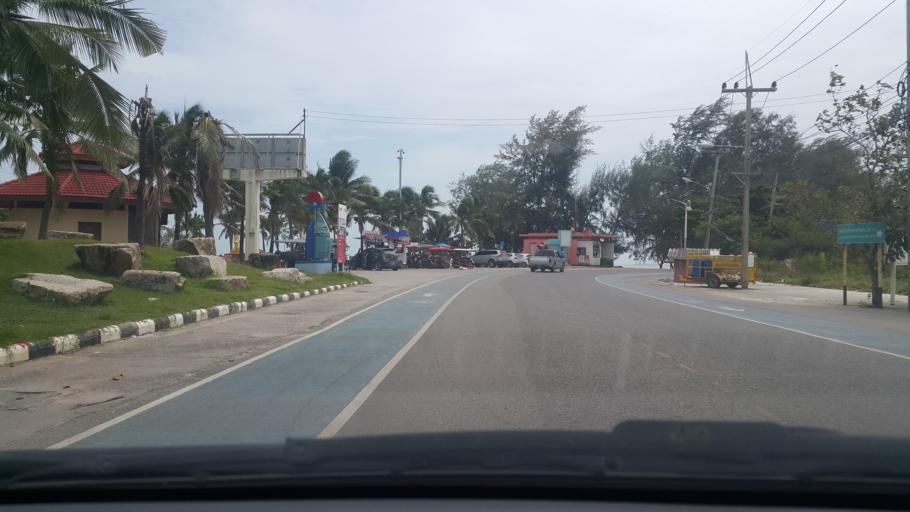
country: TH
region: Rayong
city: Rayong
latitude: 12.6111
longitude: 101.3850
